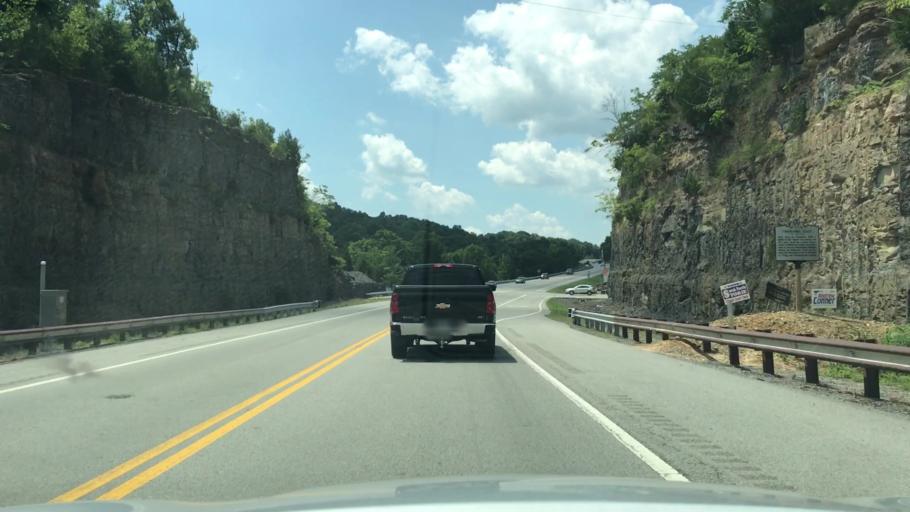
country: US
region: Tennessee
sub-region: Pickett County
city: Byrdstown
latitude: 36.5311
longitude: -85.1616
